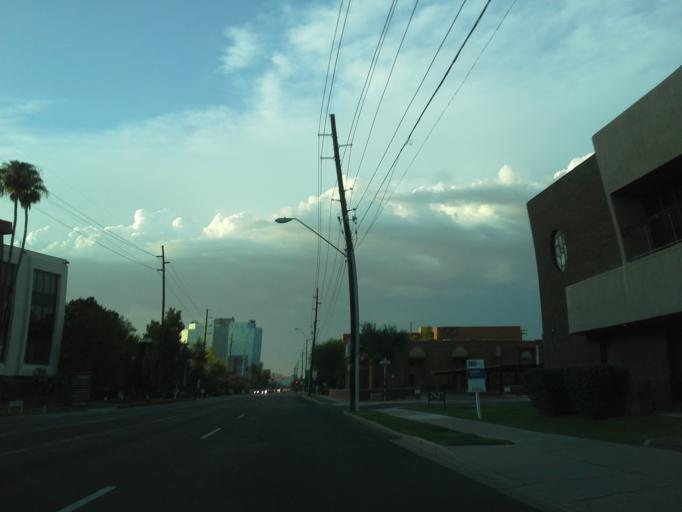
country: US
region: Arizona
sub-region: Maricopa County
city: Phoenix
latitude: 33.4776
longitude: -112.0694
